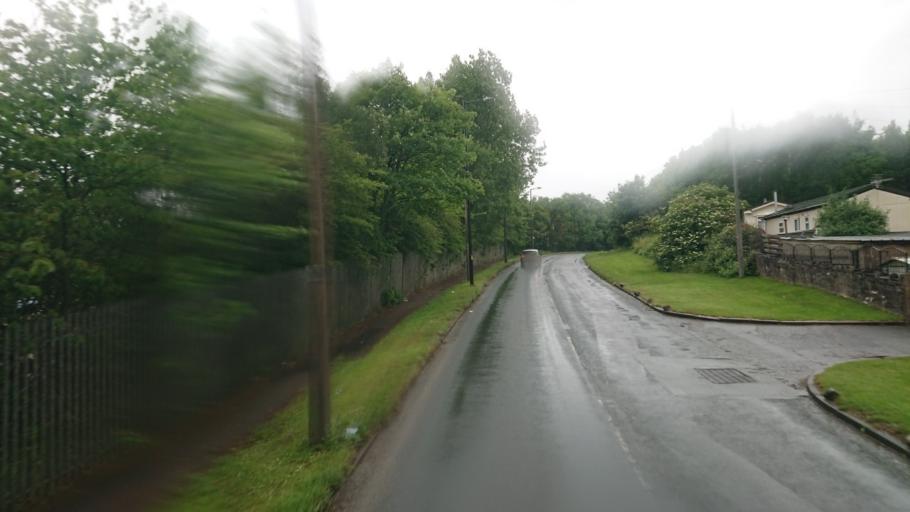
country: GB
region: England
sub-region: Lancashire
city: Morecambe
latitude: 54.0299
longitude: -2.8942
